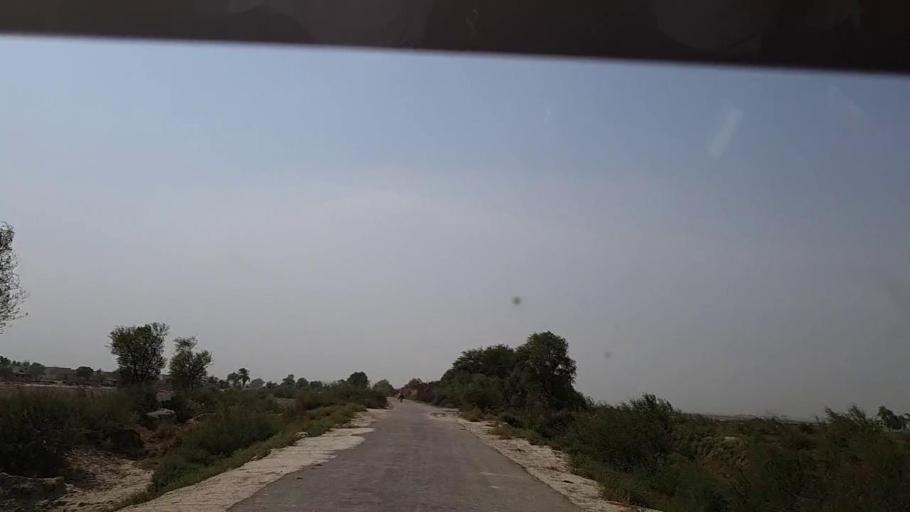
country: PK
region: Sindh
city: Khairpur Nathan Shah
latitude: 27.0339
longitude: 67.6788
